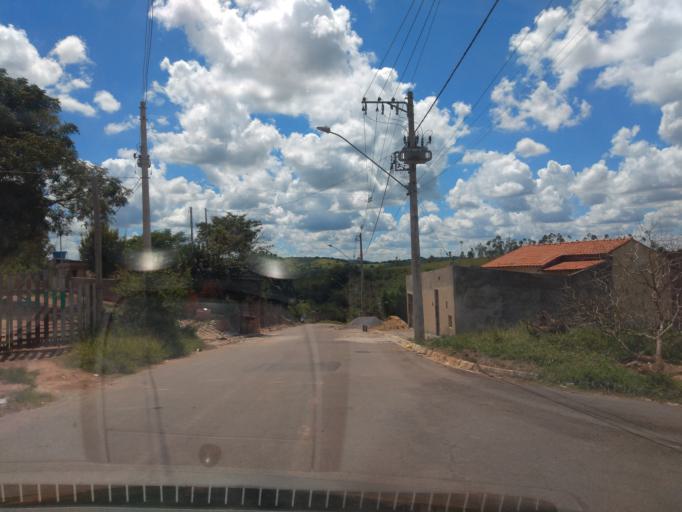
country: BR
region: Minas Gerais
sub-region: Tres Coracoes
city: Tres Coracoes
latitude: -21.6824
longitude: -45.2406
